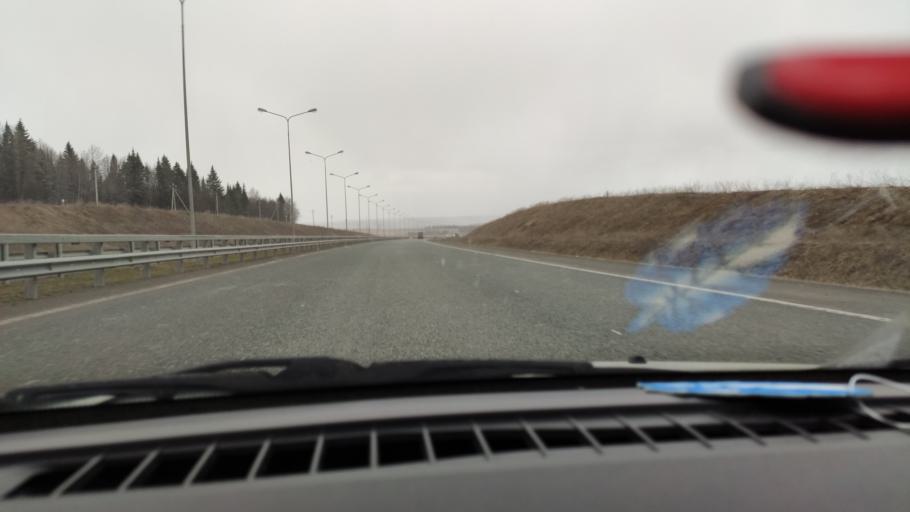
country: RU
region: Perm
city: Zvezdnyy
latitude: 57.7620
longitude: 56.3328
